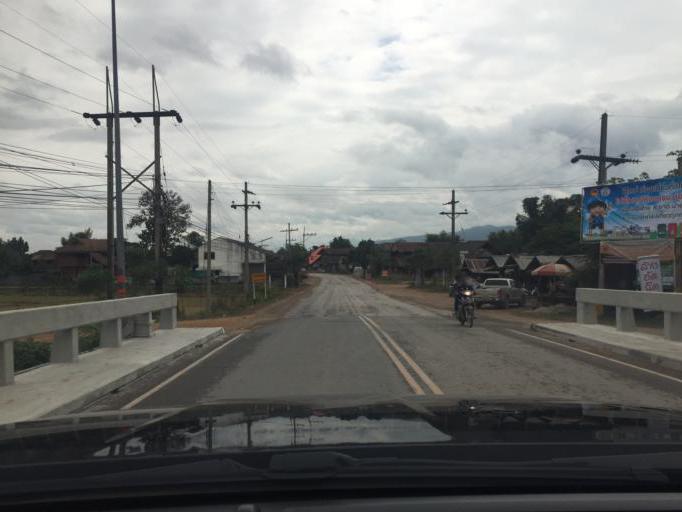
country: TH
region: Phayao
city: Pong
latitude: 19.1679
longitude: 100.2852
